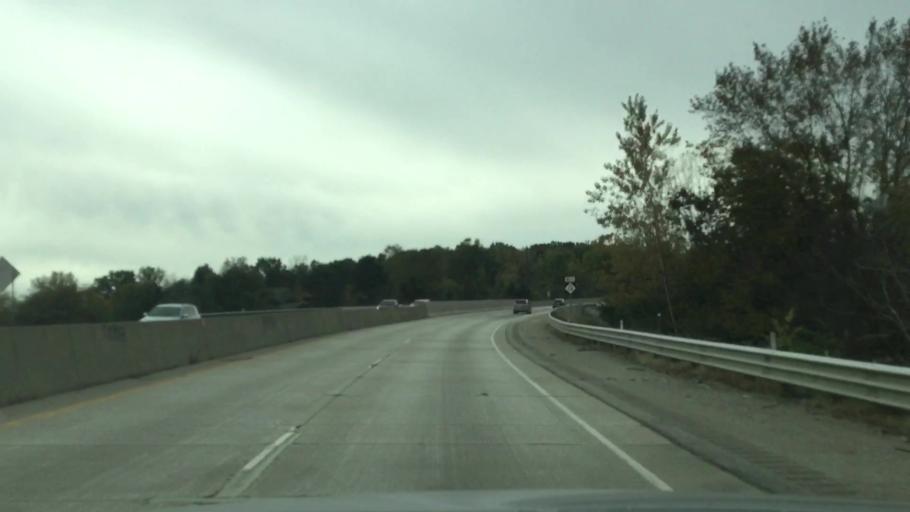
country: US
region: Michigan
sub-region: Washtenaw County
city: Ann Arbor
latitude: 42.3008
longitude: -83.7469
